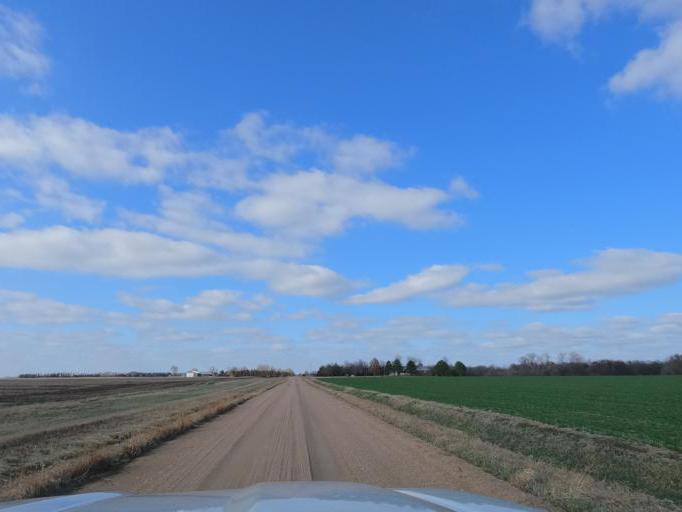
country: US
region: Kansas
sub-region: McPherson County
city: Inman
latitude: 38.2338
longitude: -97.8669
